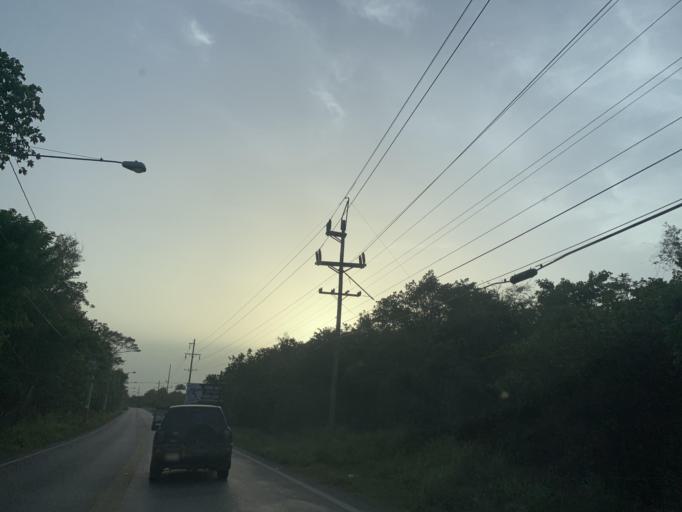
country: DO
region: Puerto Plata
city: Cabarete
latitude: 19.7786
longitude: -70.4772
